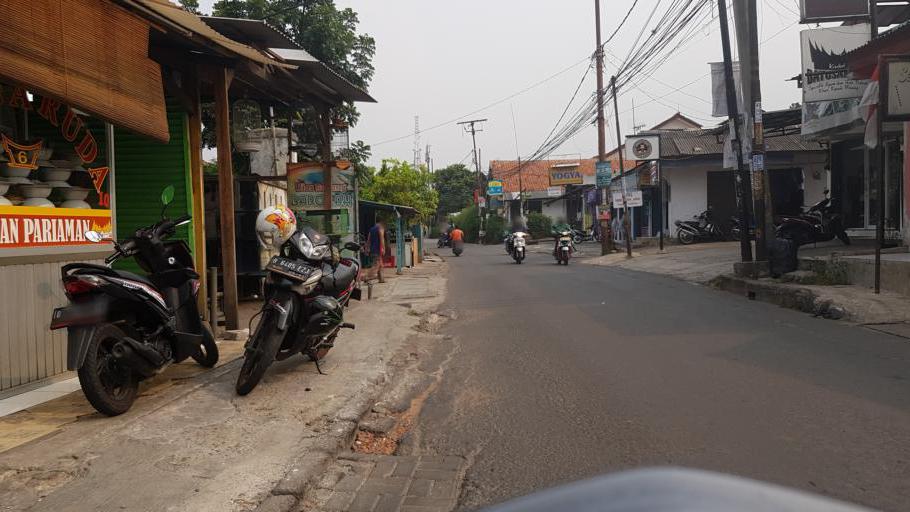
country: ID
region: West Java
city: Depok
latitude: -6.3567
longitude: 106.8429
